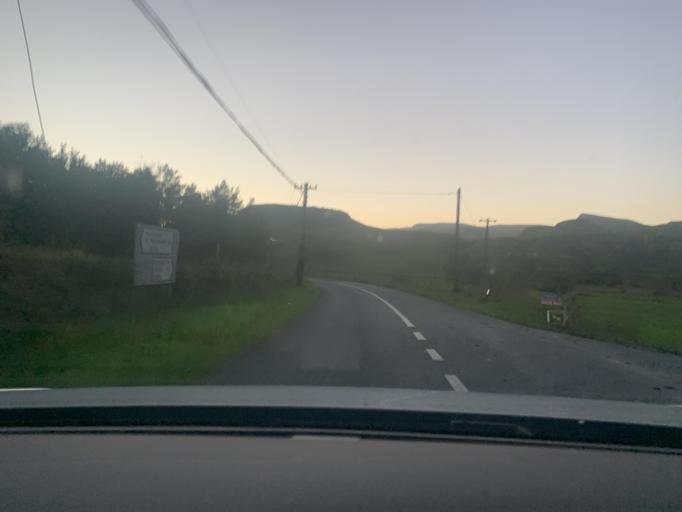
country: IE
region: Connaught
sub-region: County Leitrim
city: Manorhamilton
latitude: 54.2770
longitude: -8.2975
